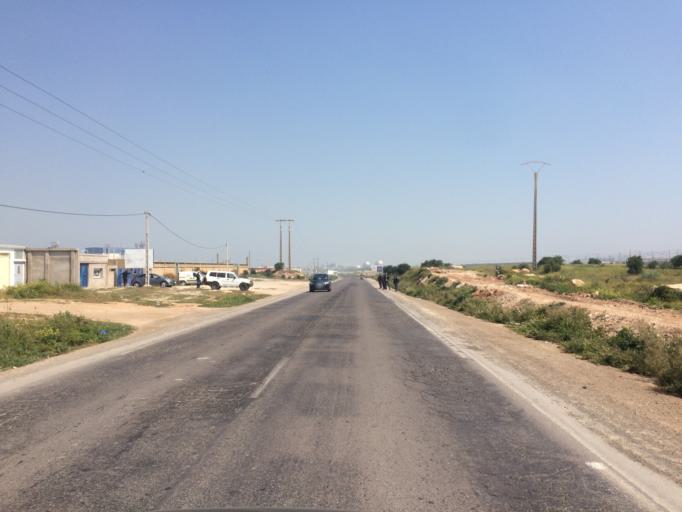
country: MA
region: Doukkala-Abda
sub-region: El-Jadida
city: Moulay Abdallah
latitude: 33.1516
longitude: -8.6054
